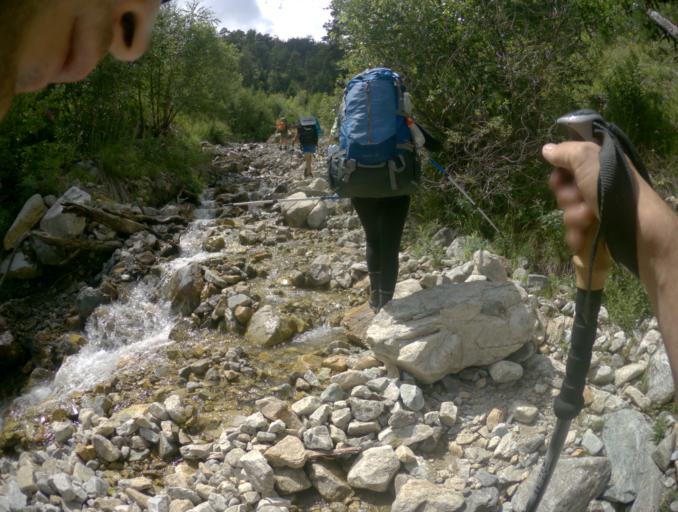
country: RU
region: Karachayevo-Cherkesiya
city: Uchkulan
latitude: 43.3498
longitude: 42.1514
